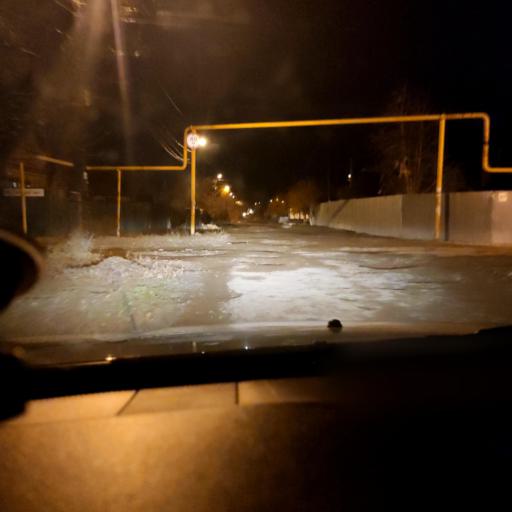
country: RU
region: Samara
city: Smyshlyayevka
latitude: 53.2335
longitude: 50.3019
